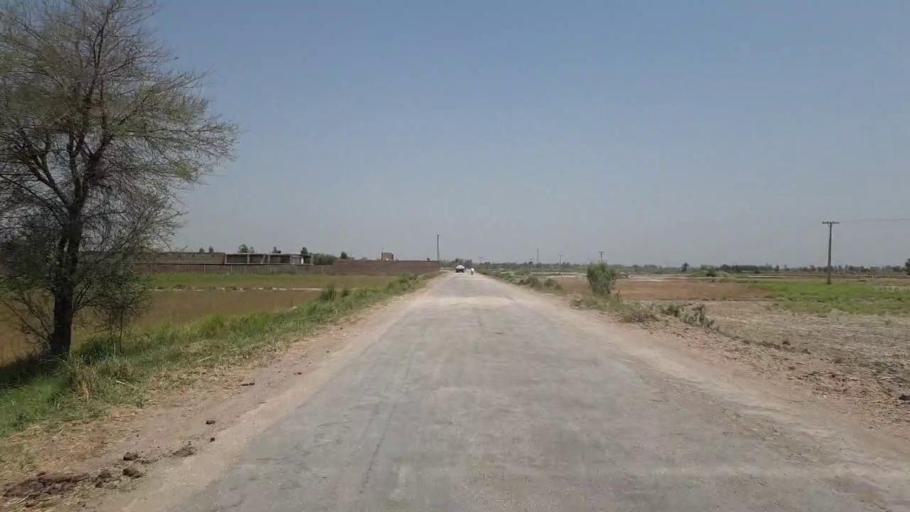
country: PK
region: Sindh
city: Adilpur
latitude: 27.8788
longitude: 69.2865
